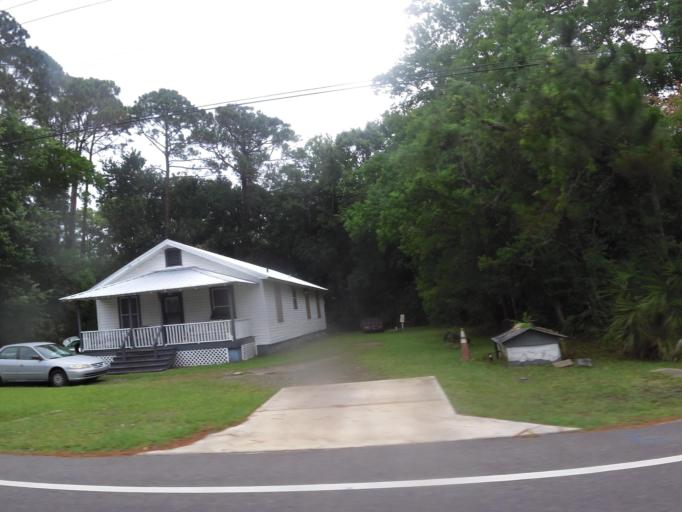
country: US
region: Florida
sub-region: Saint Johns County
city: Saint Augustine
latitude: 29.9013
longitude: -81.3499
